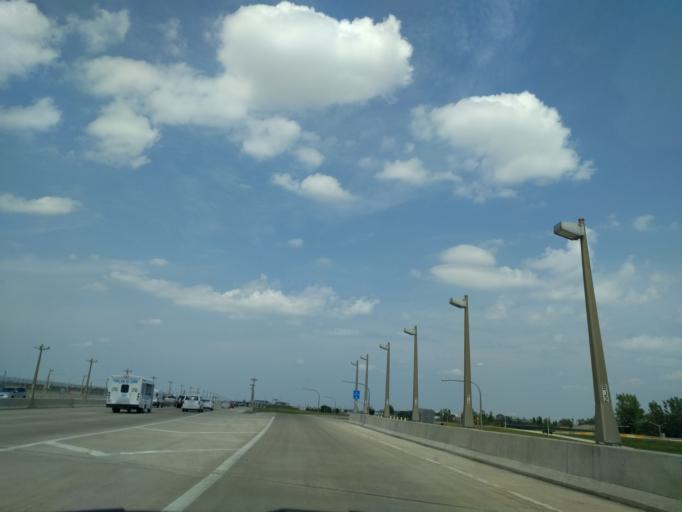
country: US
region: Illinois
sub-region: Cook County
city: Schiller Park
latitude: 41.9690
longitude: -87.8763
